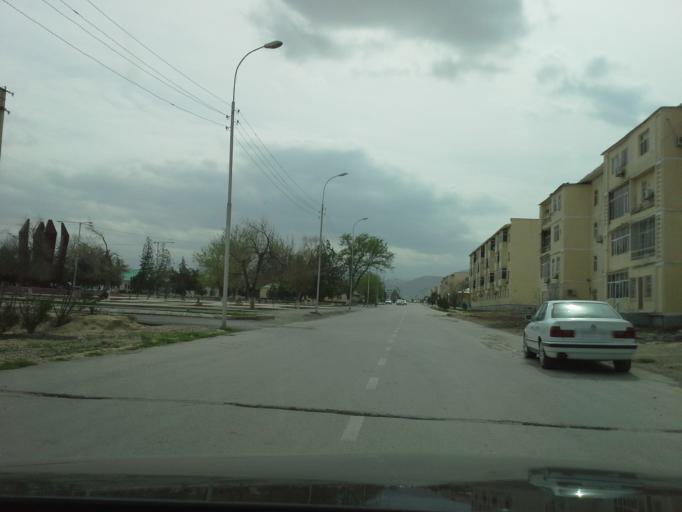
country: TM
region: Ahal
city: Abadan
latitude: 38.0623
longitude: 58.1514
